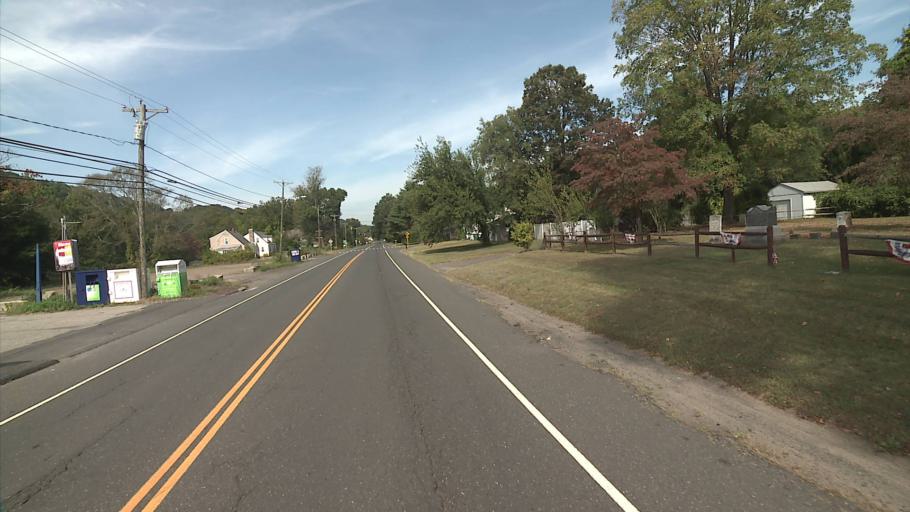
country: US
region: Connecticut
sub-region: New Haven County
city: Ansonia
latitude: 41.3676
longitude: -73.1456
